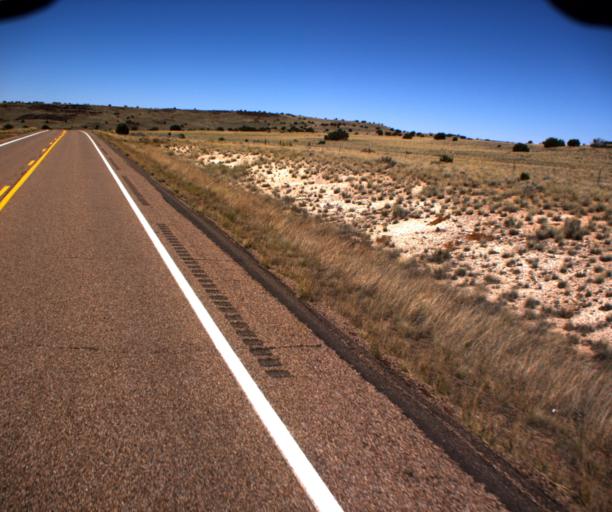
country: US
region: Arizona
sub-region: Apache County
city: Saint Johns
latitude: 34.5659
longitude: -109.5086
